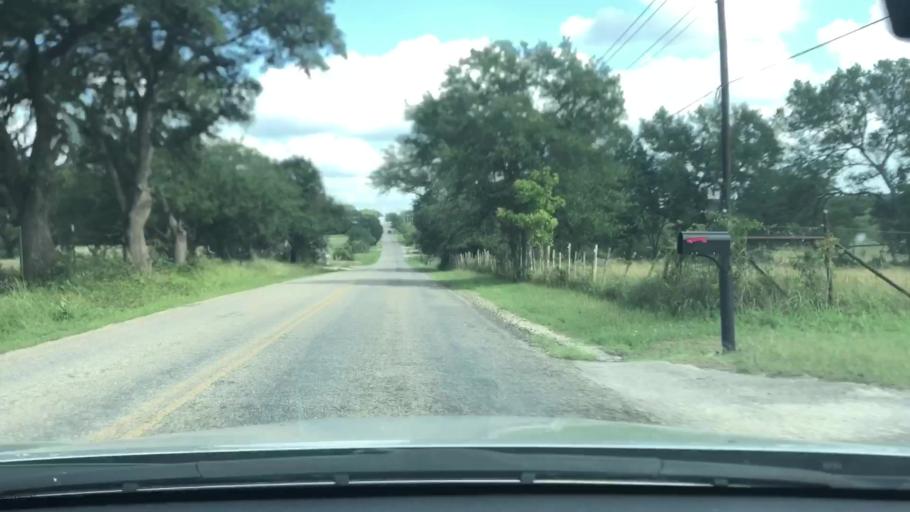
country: US
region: Texas
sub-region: Bexar County
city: Fair Oaks Ranch
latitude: 29.7862
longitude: -98.6690
